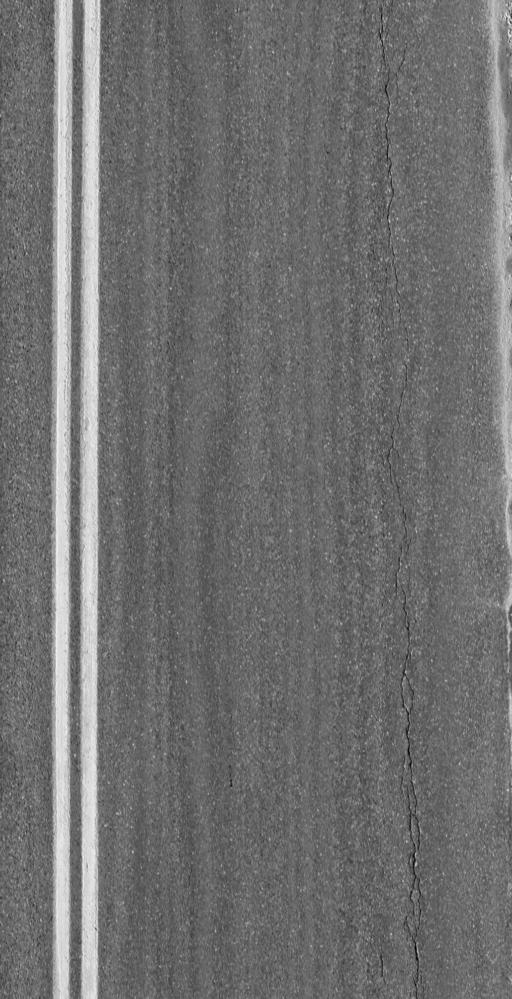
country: US
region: Vermont
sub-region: Addison County
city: Vergennes
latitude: 44.3068
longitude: -73.2871
